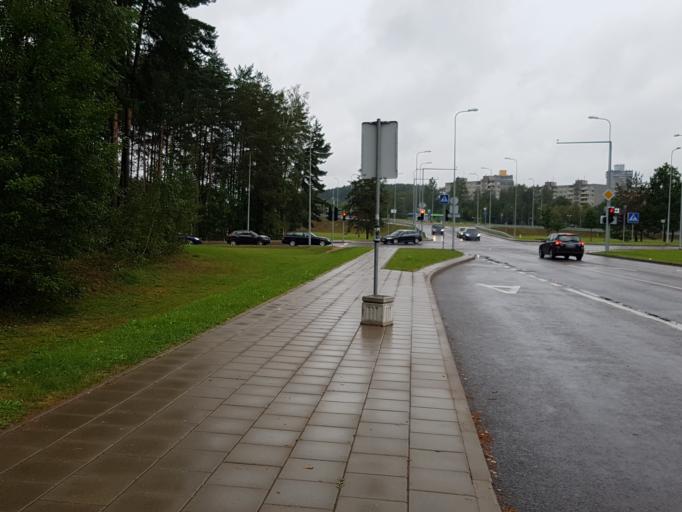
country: LT
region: Vilnius County
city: Lazdynai
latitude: 54.6693
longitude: 25.1978
